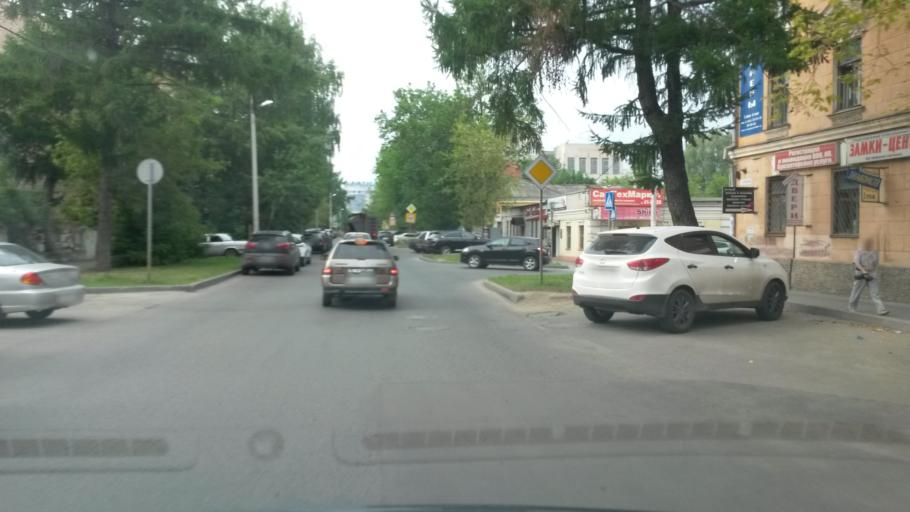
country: RU
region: Ivanovo
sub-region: Gorod Ivanovo
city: Ivanovo
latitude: 56.9946
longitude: 40.9739
